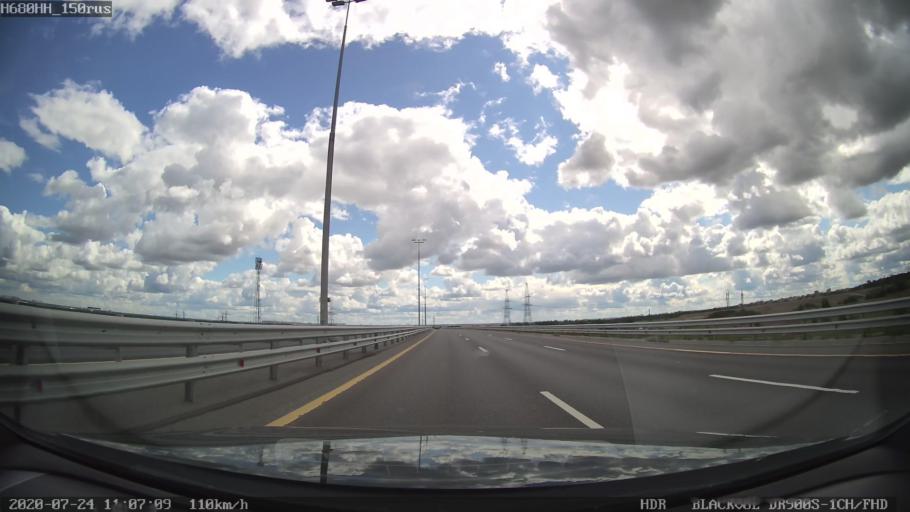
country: RU
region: St.-Petersburg
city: Pushkin
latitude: 59.7588
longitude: 30.3918
